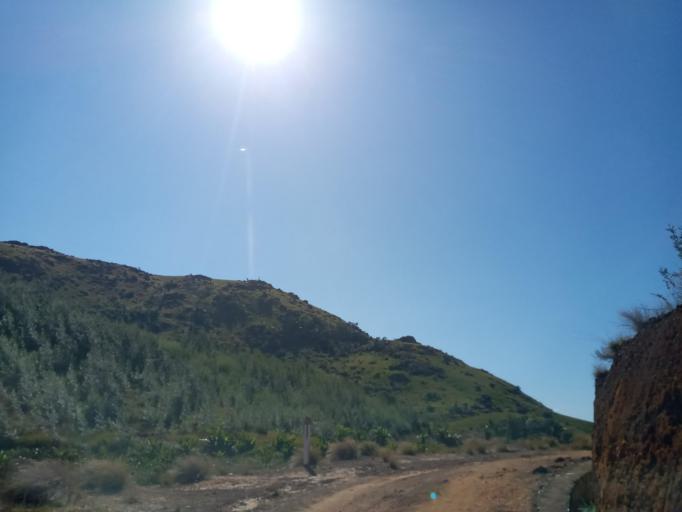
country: MG
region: Anosy
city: Fort Dauphin
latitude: -24.9128
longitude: 47.0871
